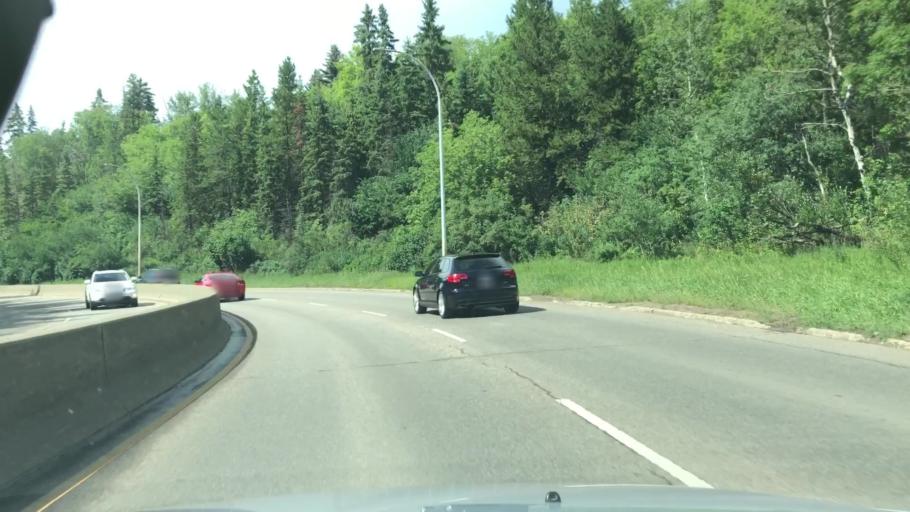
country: CA
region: Alberta
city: Edmonton
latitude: 53.5455
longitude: -113.5426
